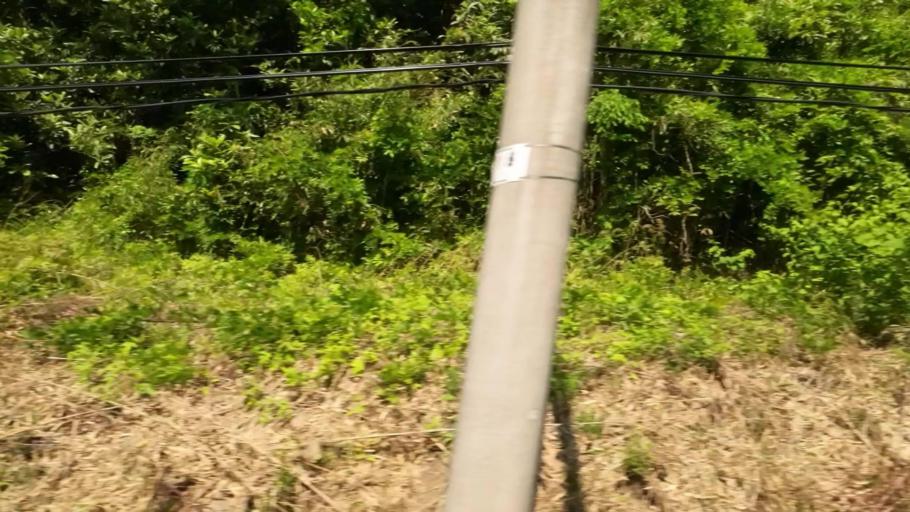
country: JP
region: Ehime
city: Kawanoecho
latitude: 34.0207
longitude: 133.5775
